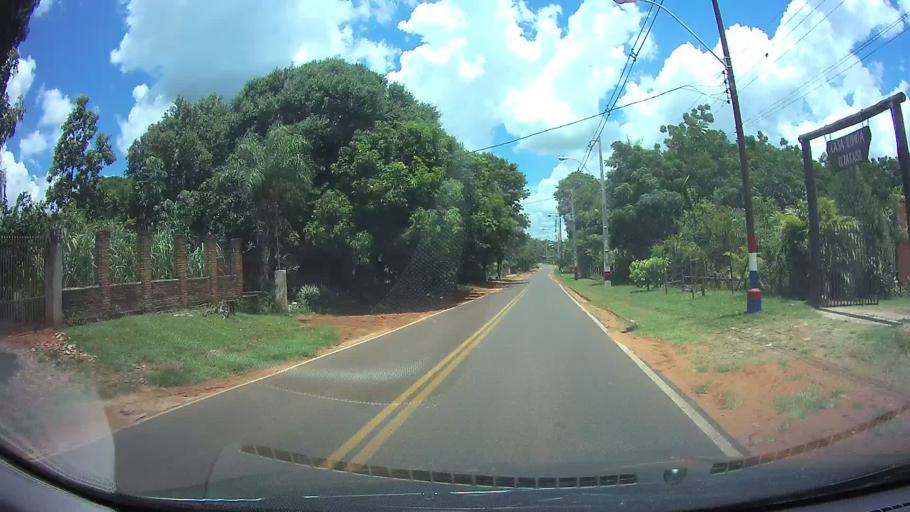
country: PY
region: Central
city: Capiata
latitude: -25.3106
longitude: -57.4333
